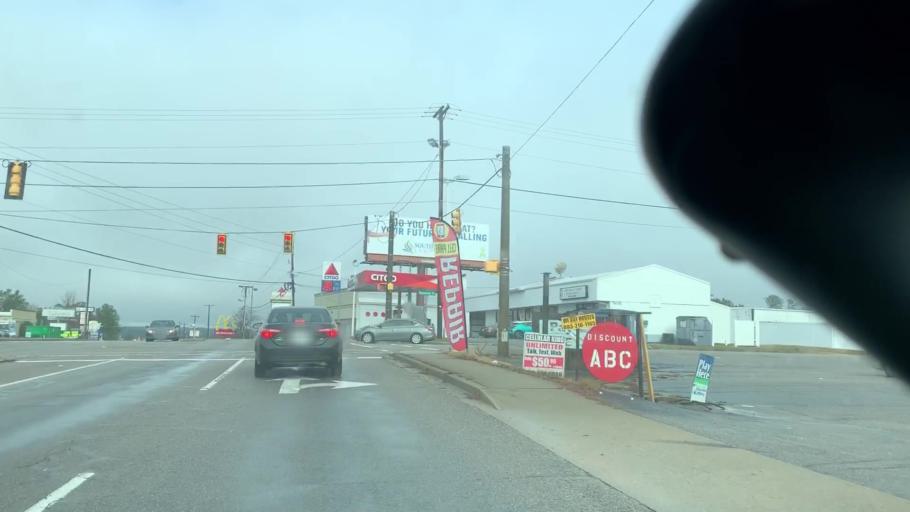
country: US
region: South Carolina
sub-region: Richland County
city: Woodfield
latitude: 34.0516
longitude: -80.9451
